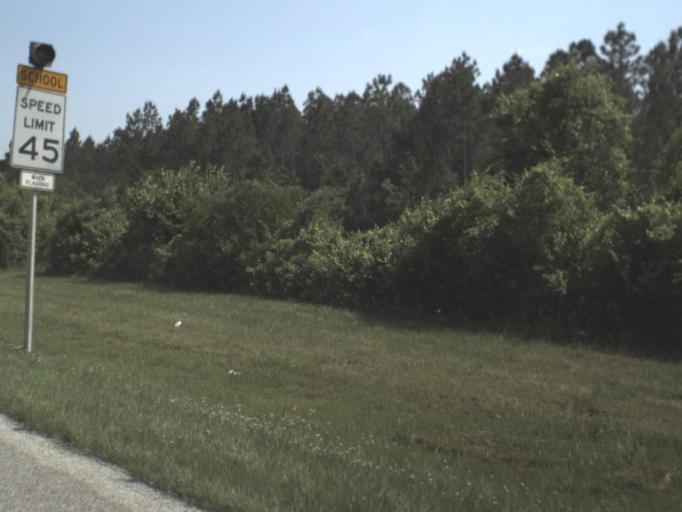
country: US
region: Florida
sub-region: Saint Johns County
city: Palm Valley
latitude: 30.0782
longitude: -81.4522
